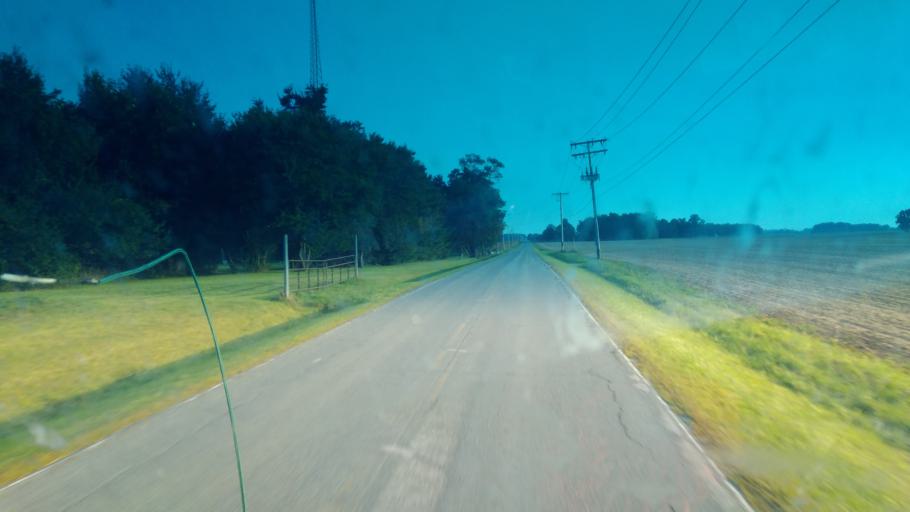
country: US
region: Ohio
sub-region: Crawford County
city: Crestline
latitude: 40.8201
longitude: -82.8188
